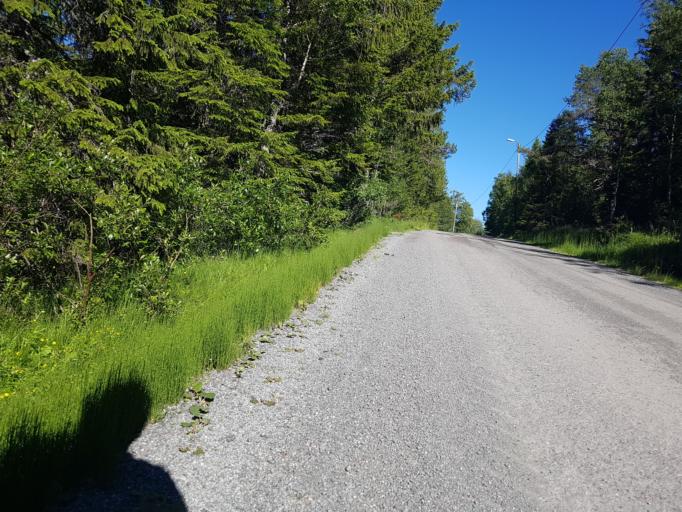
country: NO
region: Sor-Trondelag
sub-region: Trondheim
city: Trondheim
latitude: 63.4333
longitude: 10.2733
